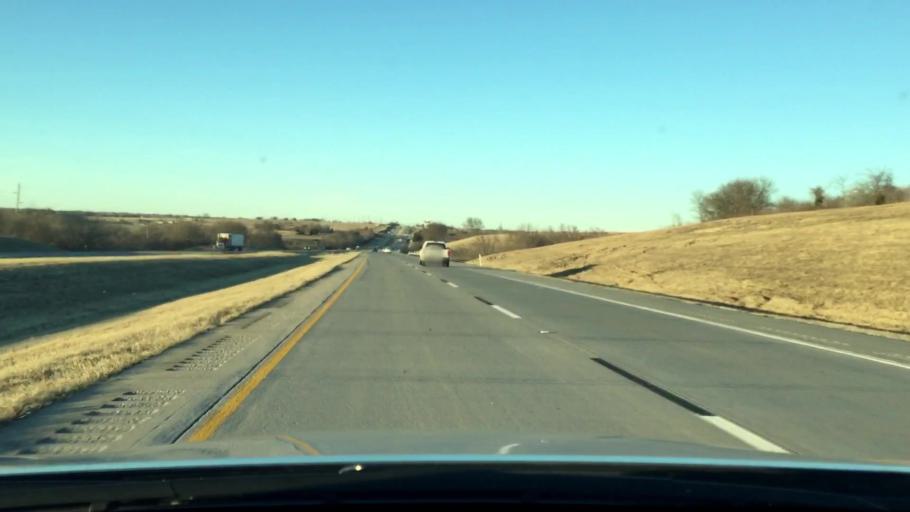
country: US
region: Oklahoma
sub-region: Love County
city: Marietta
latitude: 33.8707
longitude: -97.1341
